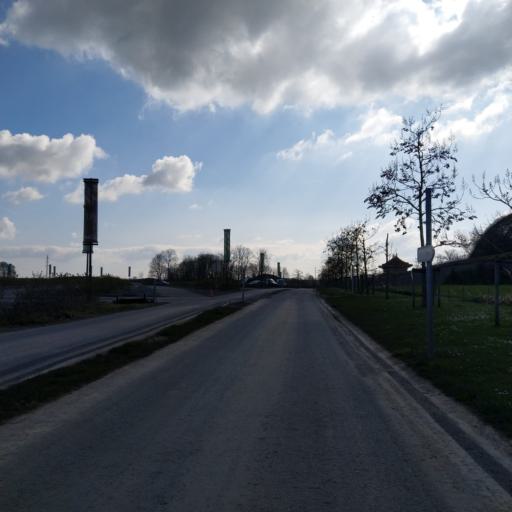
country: BE
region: Wallonia
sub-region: Province du Hainaut
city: Lens
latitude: 50.5866
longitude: 3.8898
